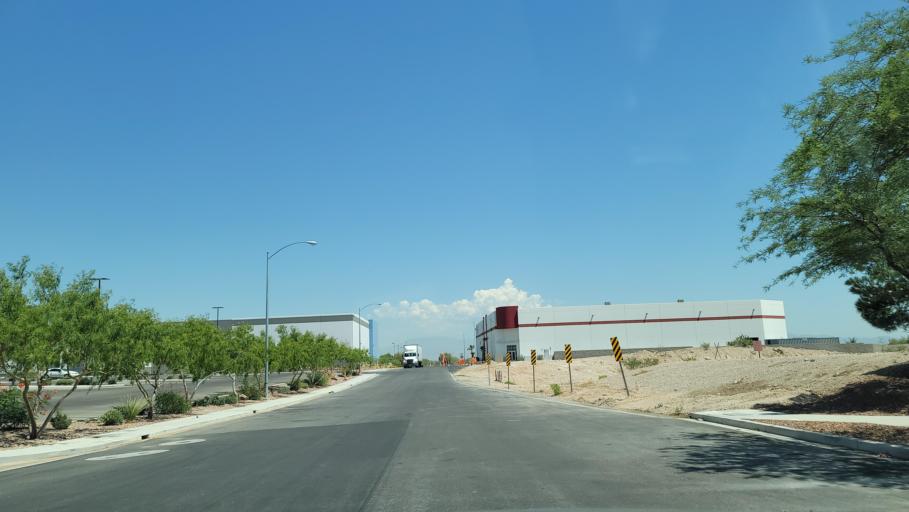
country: US
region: Nevada
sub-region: Clark County
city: Spring Valley
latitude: 36.0721
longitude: -115.2403
